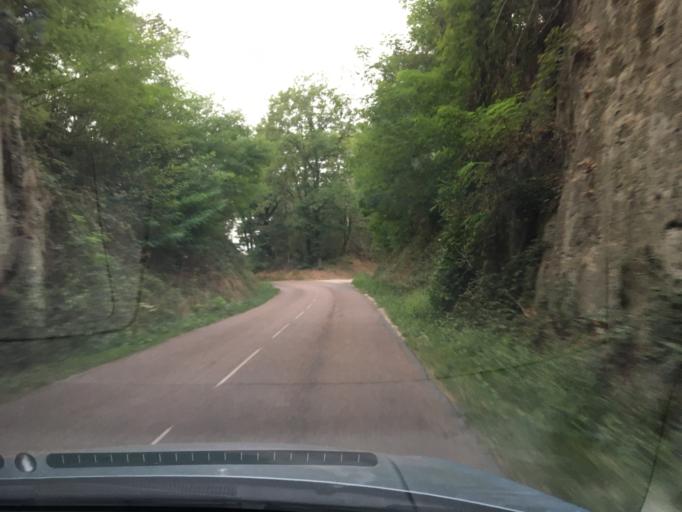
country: FR
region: Bourgogne
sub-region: Departement de l'Yonne
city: Appoigny
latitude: 47.8734
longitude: 3.5104
